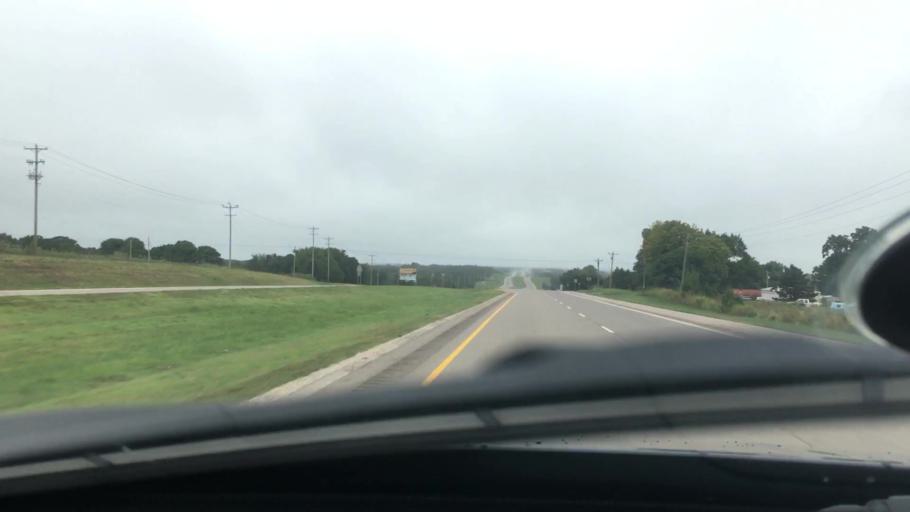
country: US
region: Oklahoma
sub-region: Seminole County
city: Seminole
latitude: 35.3168
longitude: -96.6713
